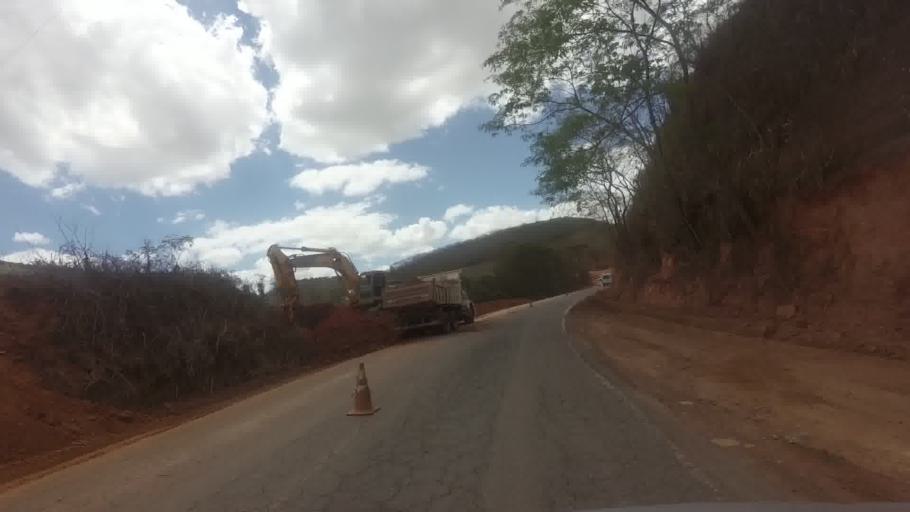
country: BR
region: Rio de Janeiro
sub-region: Santo Antonio De Padua
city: Santo Antonio de Padua
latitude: -21.5184
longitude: -42.1034
